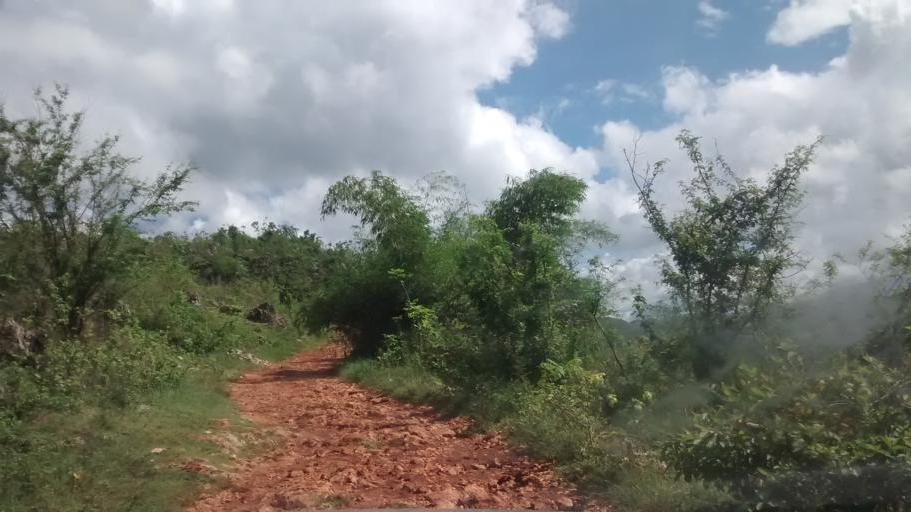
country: HT
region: Grandans
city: Corail
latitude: 18.5400
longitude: -73.9217
